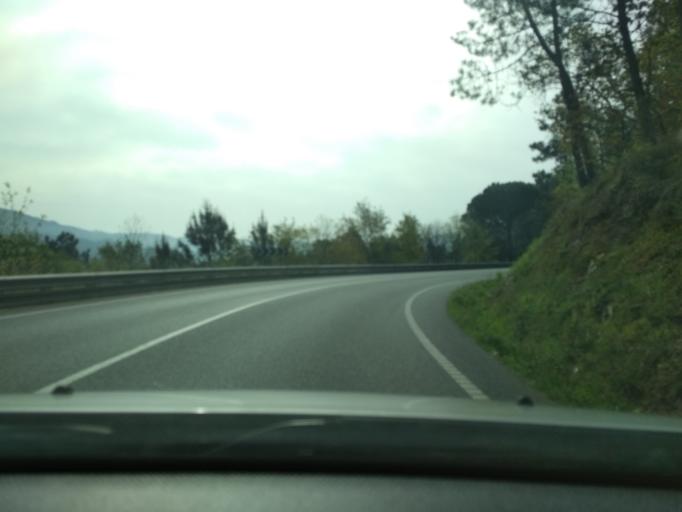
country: ES
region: Galicia
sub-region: Provincia de Pontevedra
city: Catoira
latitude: 42.6753
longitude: -8.7156
